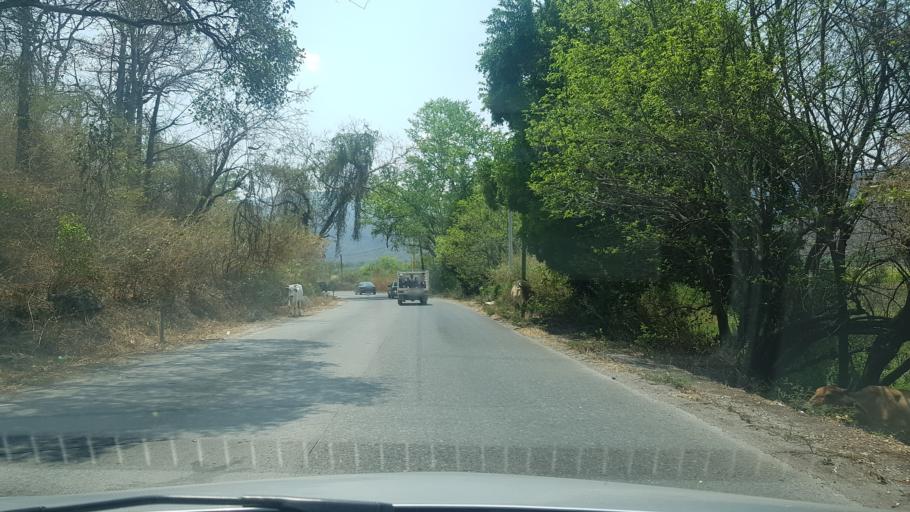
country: MX
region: Morelos
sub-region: Jiutepec
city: Independencia
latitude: 18.8003
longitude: -99.0993
